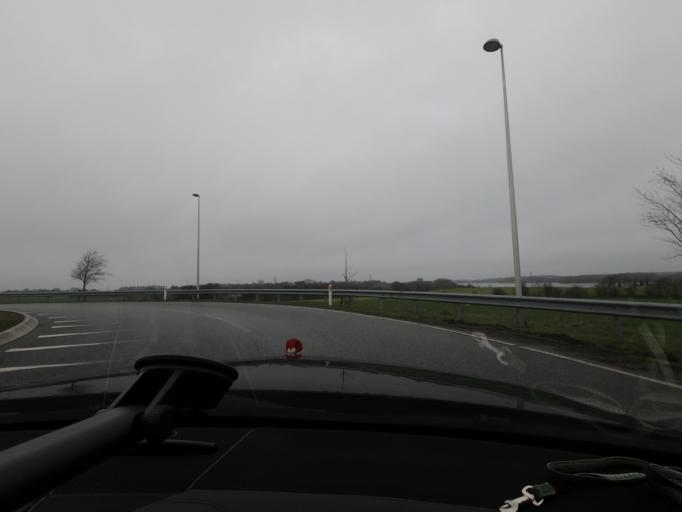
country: DK
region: South Denmark
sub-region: Sonderborg Kommune
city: Dybbol
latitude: 54.9216
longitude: 9.7538
